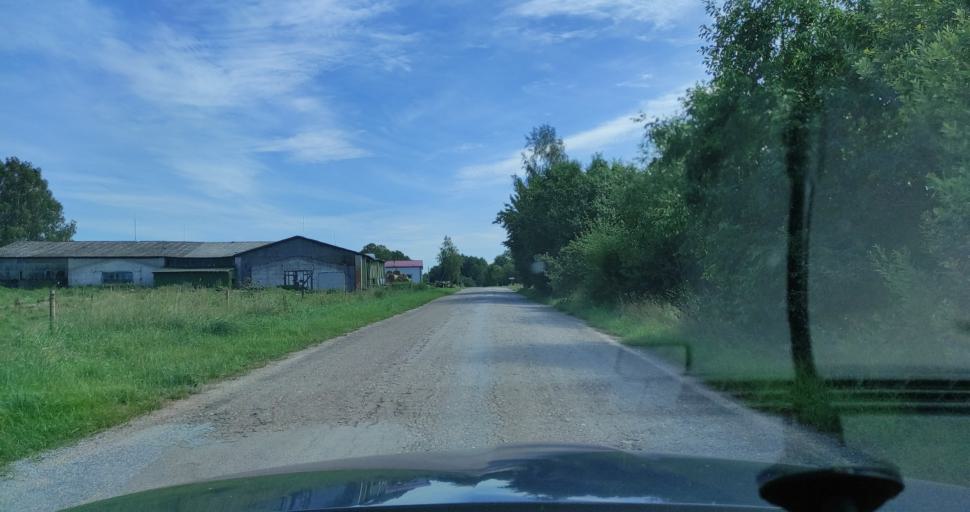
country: LV
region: Durbe
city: Liegi
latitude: 56.7471
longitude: 21.3673
